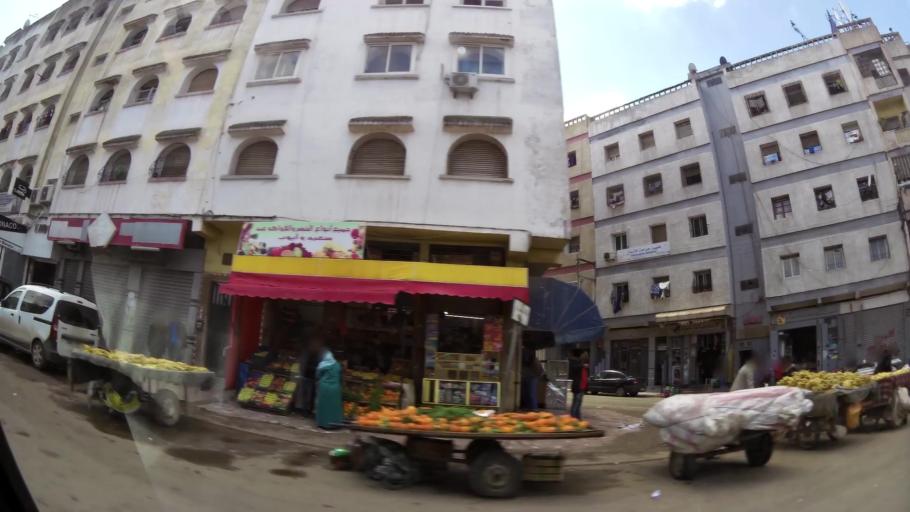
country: MA
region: Grand Casablanca
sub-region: Mediouna
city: Tit Mellil
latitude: 33.5383
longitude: -7.5539
